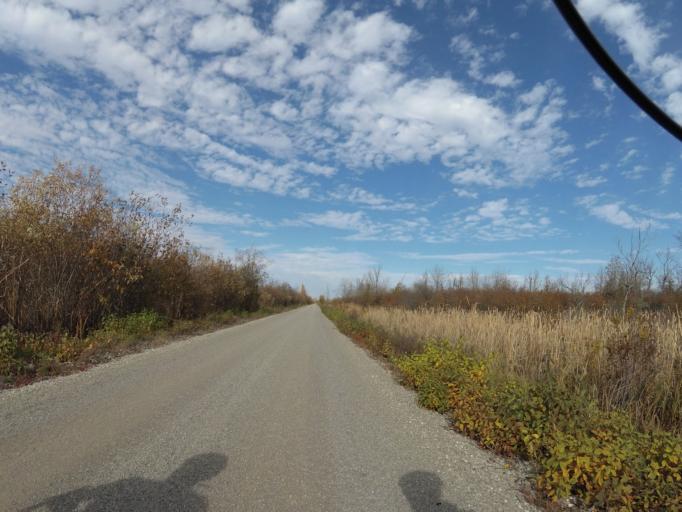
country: CA
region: Ontario
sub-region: Lanark County
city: Smiths Falls
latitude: 45.0206
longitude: -76.0752
